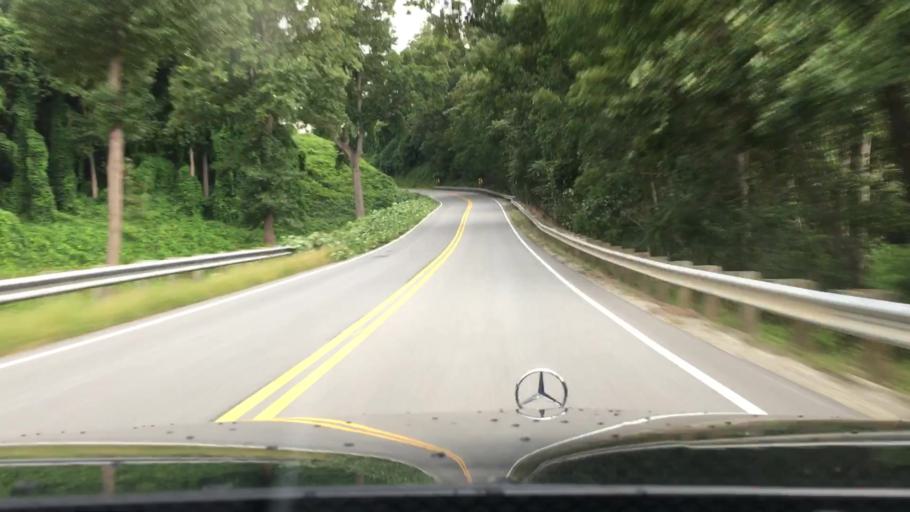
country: US
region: Virginia
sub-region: Nelson County
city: Lovingston
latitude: 37.7958
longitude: -78.9689
